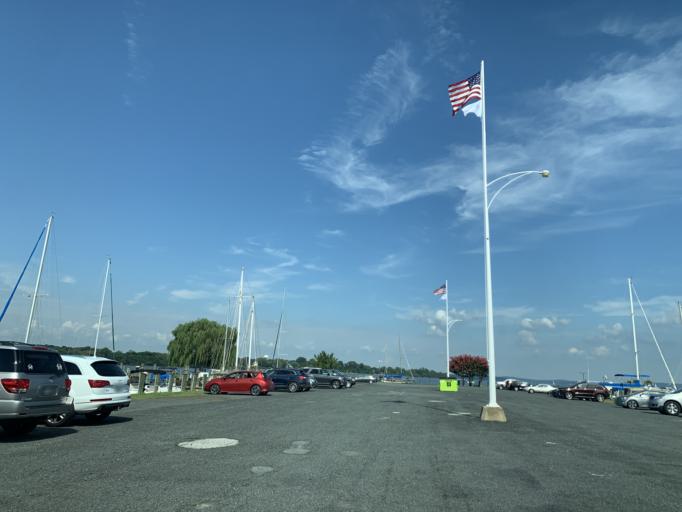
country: US
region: Maryland
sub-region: Harford County
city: Havre de Grace
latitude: 39.5467
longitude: -76.0857
